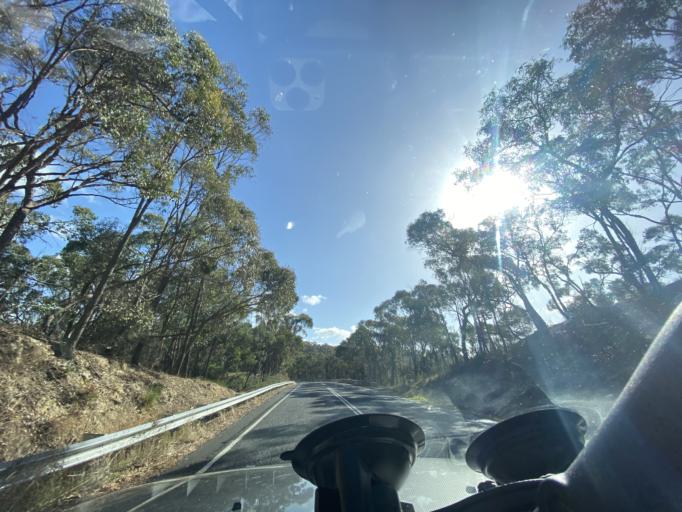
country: AU
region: Victoria
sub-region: Murrindindi
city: Kinglake West
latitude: -37.3010
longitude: 145.3756
